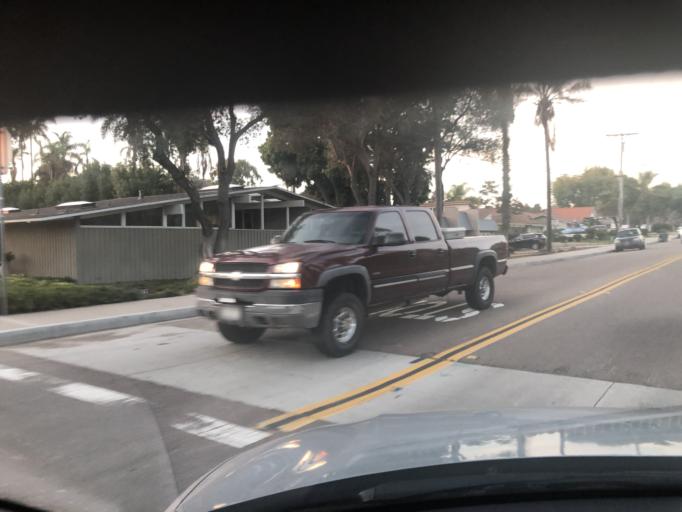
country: US
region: California
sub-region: San Diego County
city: Chula Vista
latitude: 32.6413
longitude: -117.0663
